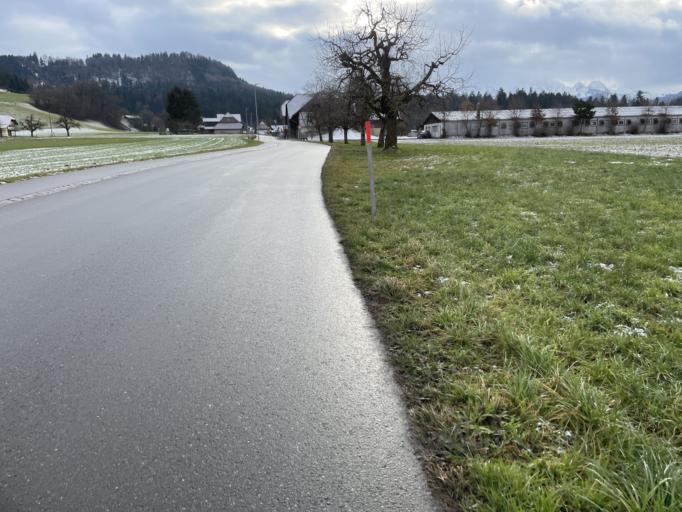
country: CH
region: Bern
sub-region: Thun District
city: Heimberg
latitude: 46.8148
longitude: 7.6140
